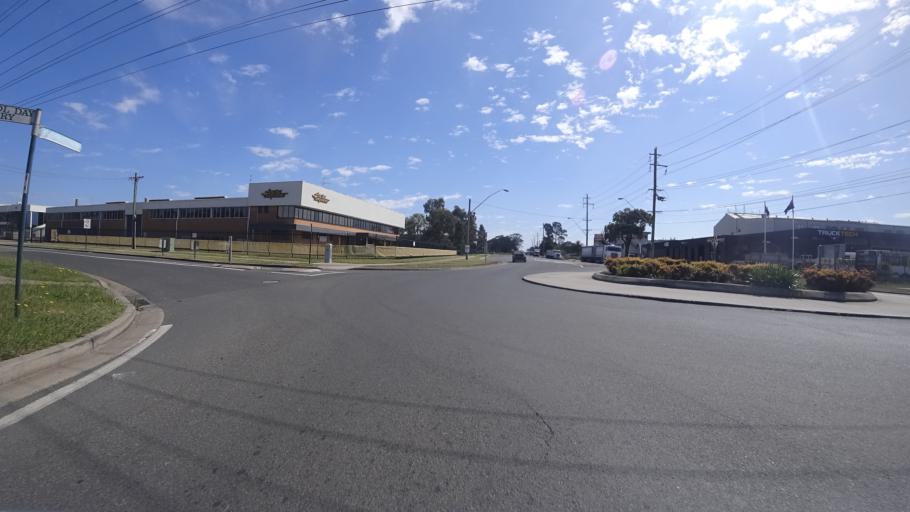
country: AU
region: New South Wales
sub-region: Bankstown
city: Milperra
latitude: -33.9233
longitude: 150.9620
